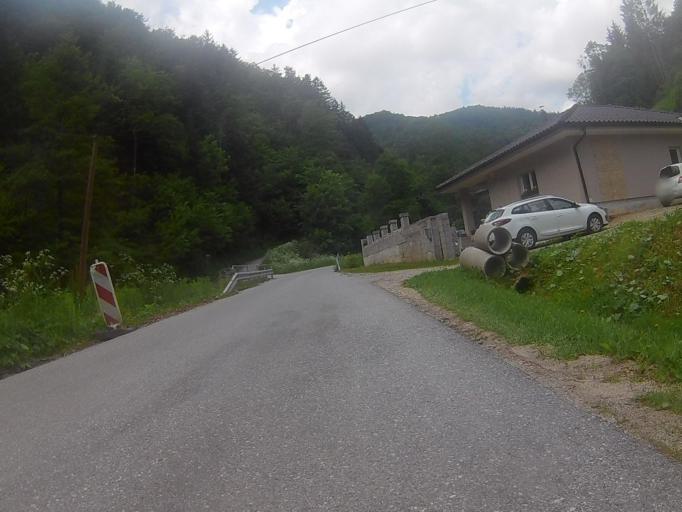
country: SI
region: Maribor
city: Bresternica
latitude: 46.5894
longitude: 15.5588
